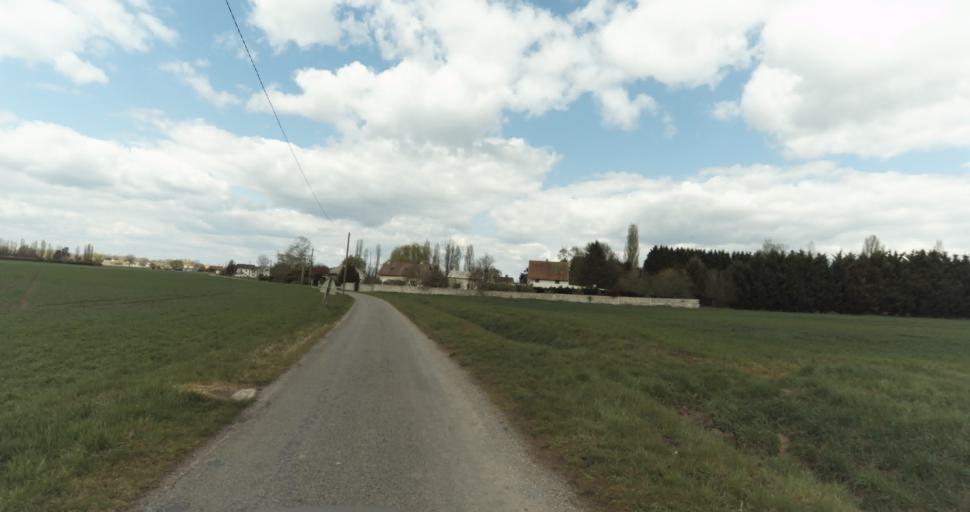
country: FR
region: Bourgogne
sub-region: Departement de la Cote-d'Or
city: Auxonne
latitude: 47.1743
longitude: 5.3951
